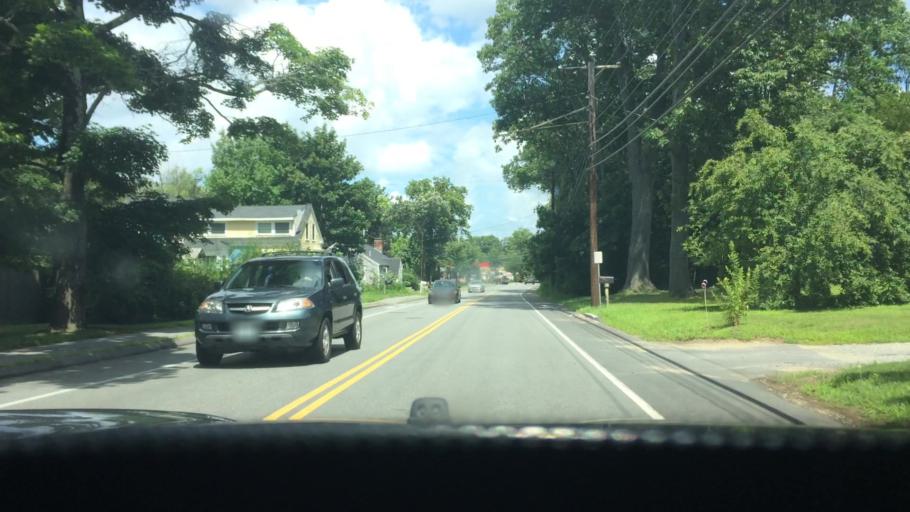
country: US
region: Massachusetts
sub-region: Middlesex County
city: Acton
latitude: 42.4657
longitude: -71.4565
